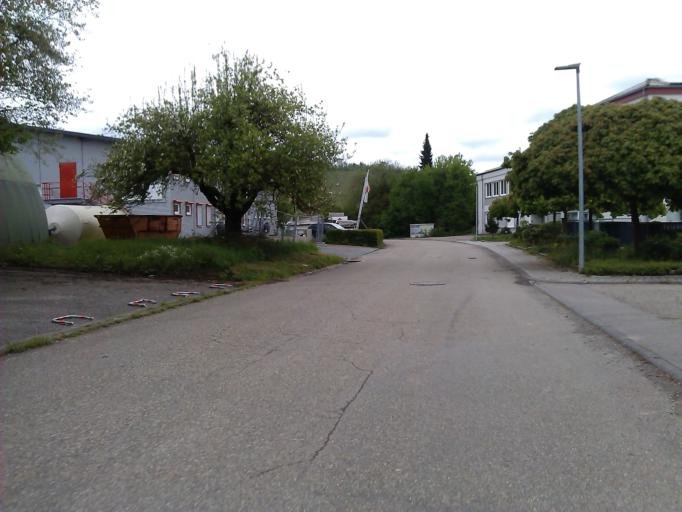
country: DE
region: Baden-Wuerttemberg
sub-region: Regierungsbezirk Stuttgart
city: Pfaffenhofen
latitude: 49.0590
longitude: 8.9773
